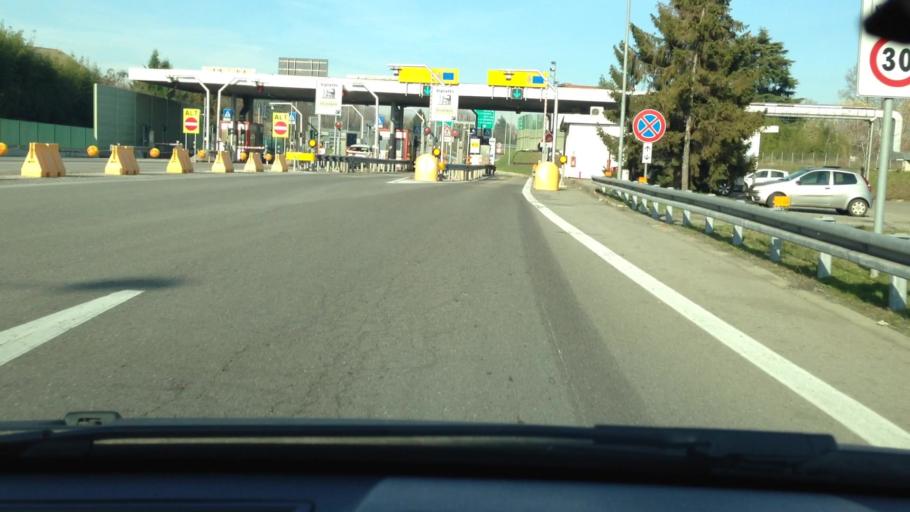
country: IT
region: Piedmont
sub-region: Provincia di Asti
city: Asti
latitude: 44.9050
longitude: 8.1764
